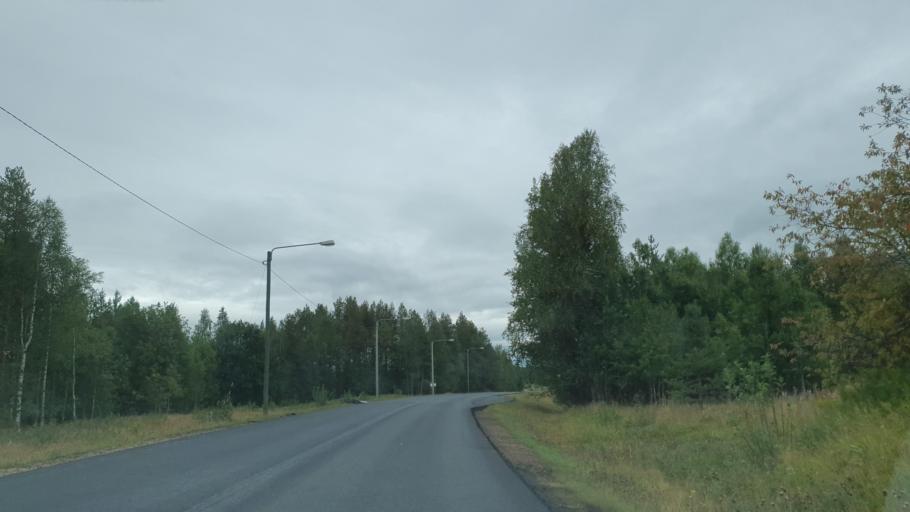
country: FI
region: Lapland
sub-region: Rovaniemi
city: Rovaniemi
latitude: 66.7790
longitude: 25.4267
